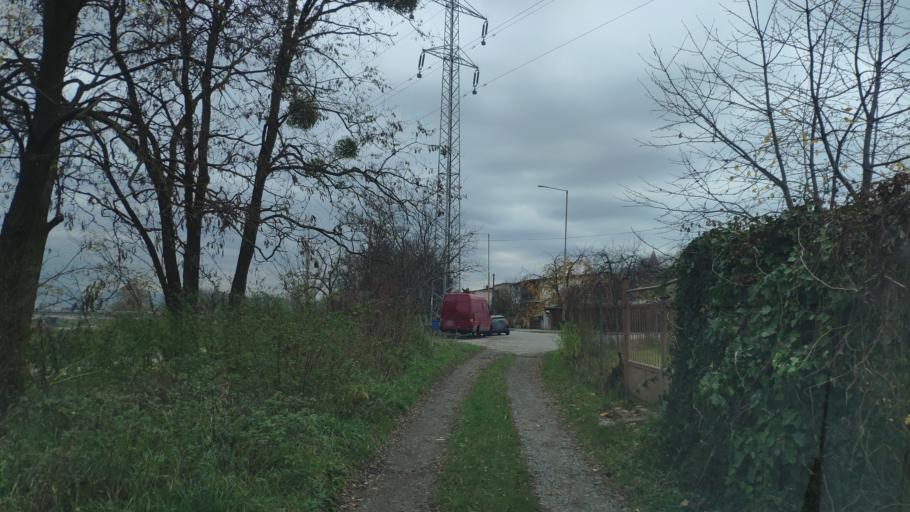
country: SK
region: Kosicky
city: Kosice
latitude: 48.6973
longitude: 21.2866
